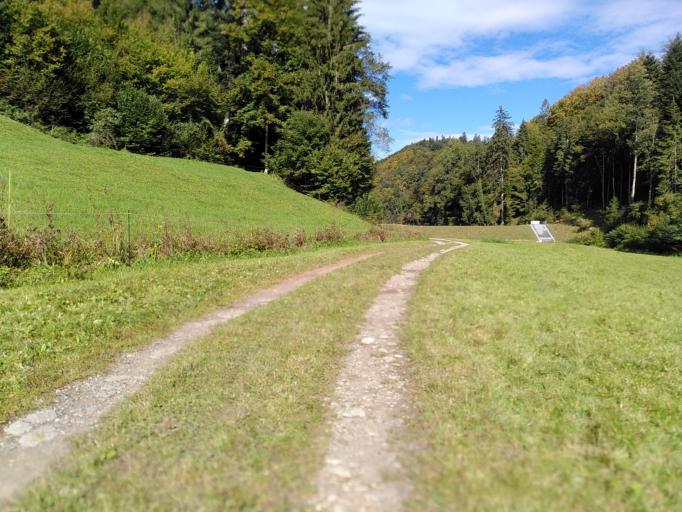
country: CH
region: Bern
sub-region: Oberaargau
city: Seeberg
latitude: 47.1344
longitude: 7.7032
